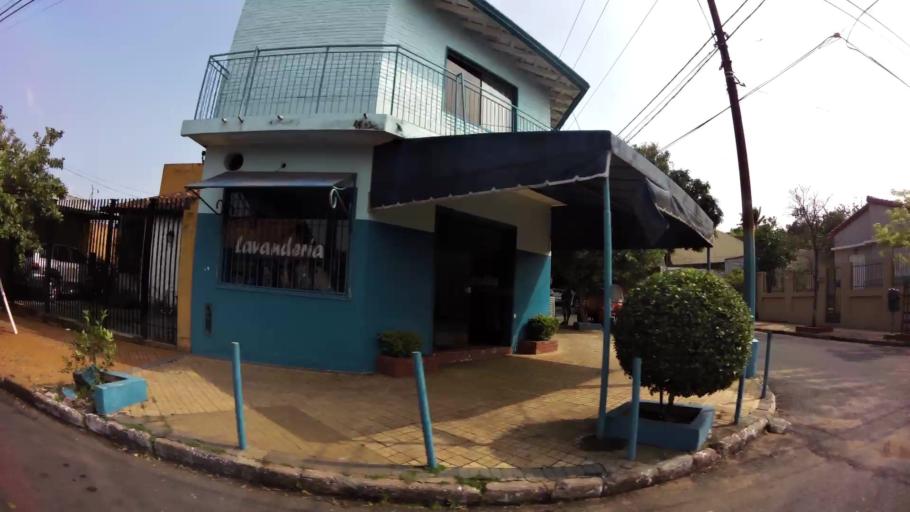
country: PY
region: Presidente Hayes
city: Nanawa
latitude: -25.2916
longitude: -57.6658
